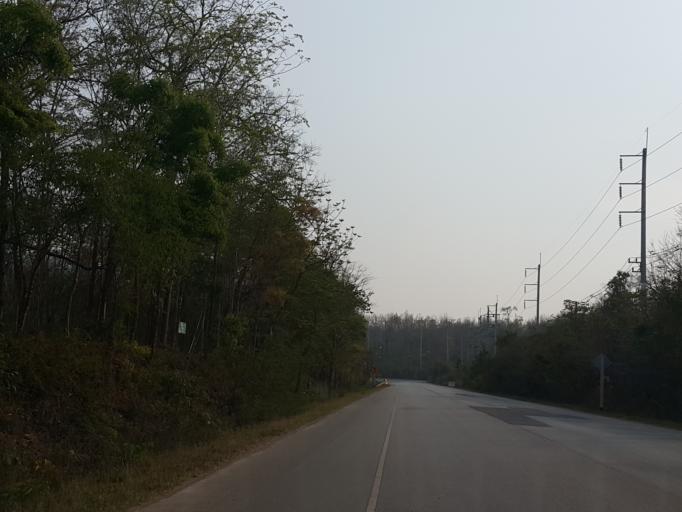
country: TH
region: Lampang
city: Chae Hom
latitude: 18.5467
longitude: 99.5683
